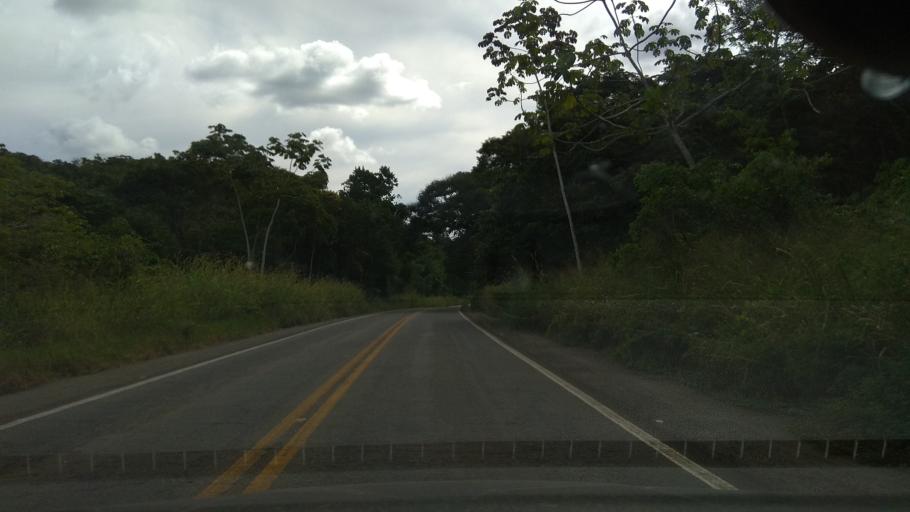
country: BR
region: Bahia
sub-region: Ibirapitanga
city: Ibirapitanga
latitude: -14.2344
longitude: -39.4261
